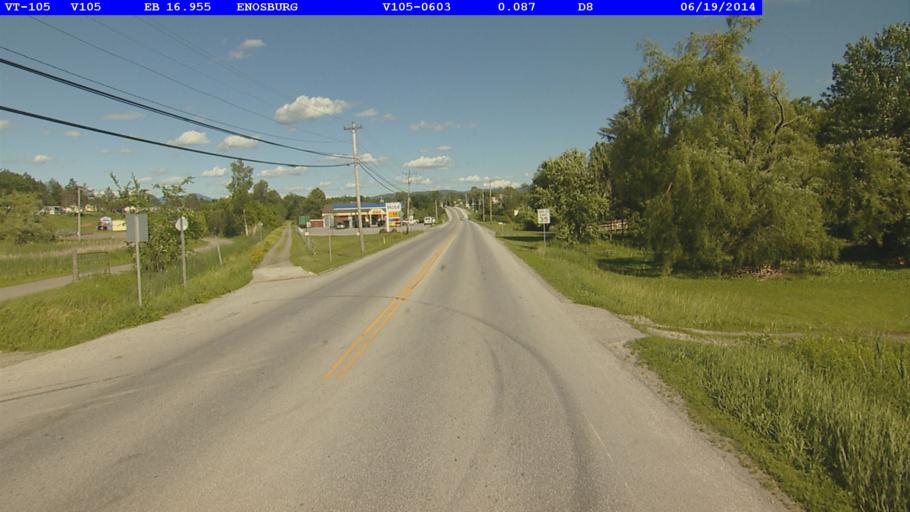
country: US
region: Vermont
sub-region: Franklin County
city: Enosburg Falls
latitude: 44.9072
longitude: -72.8179
